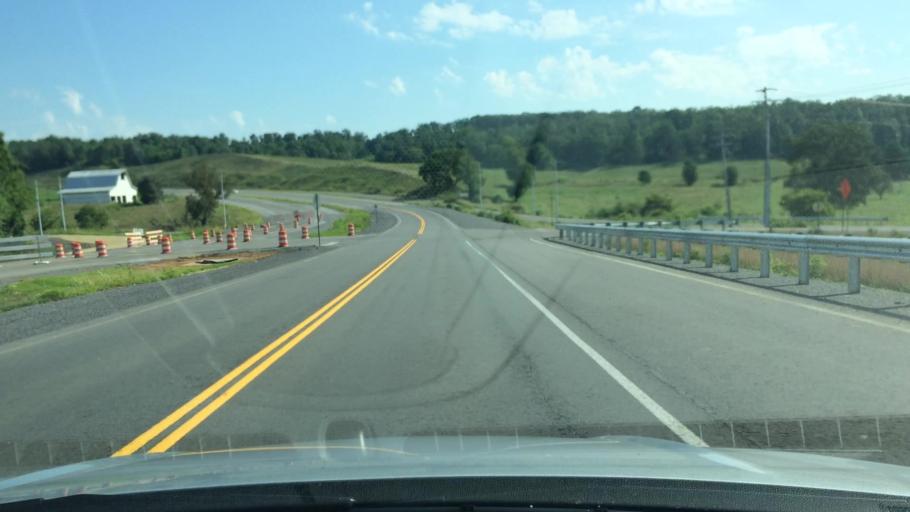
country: US
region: Tennessee
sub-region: Jefferson County
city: White Pine
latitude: 36.1226
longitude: -83.3352
